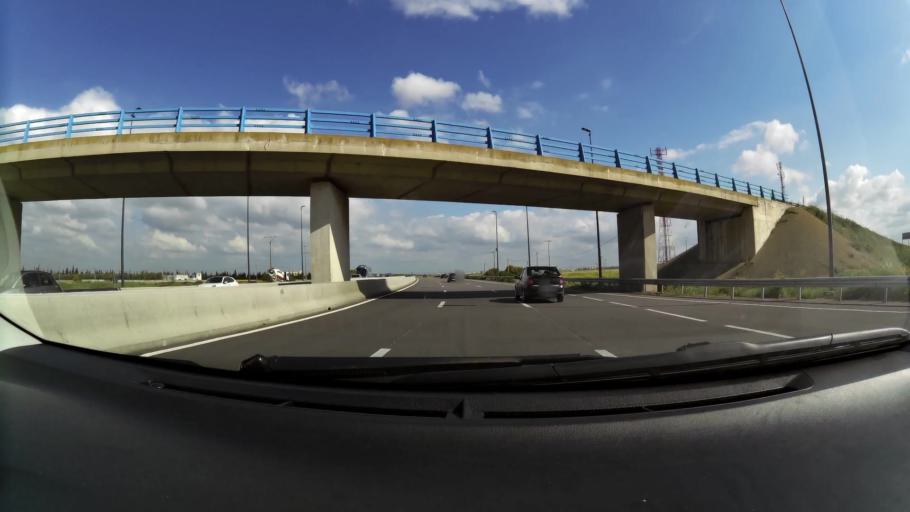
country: MA
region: Chaouia-Ouardigha
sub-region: Settat Province
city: Berrechid
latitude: 33.3172
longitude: -7.6020
